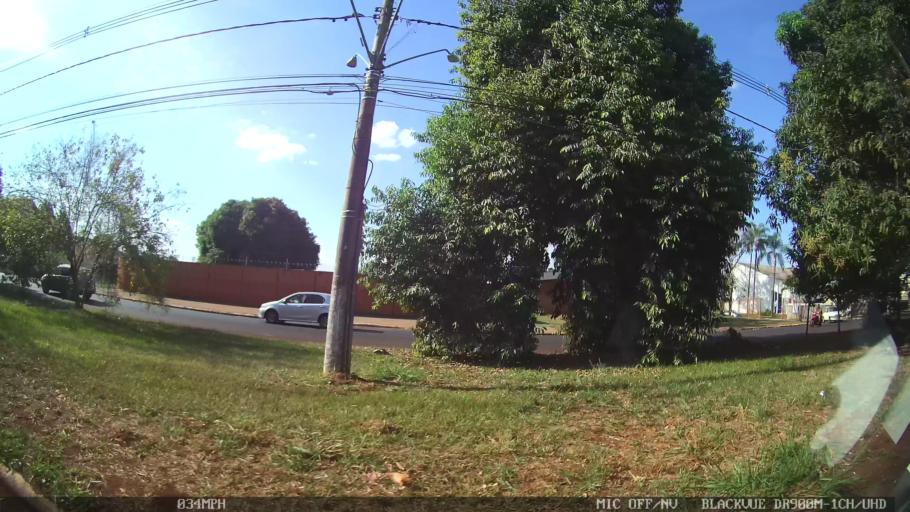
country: BR
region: Sao Paulo
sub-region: Ribeirao Preto
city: Ribeirao Preto
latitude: -21.1914
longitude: -47.7636
